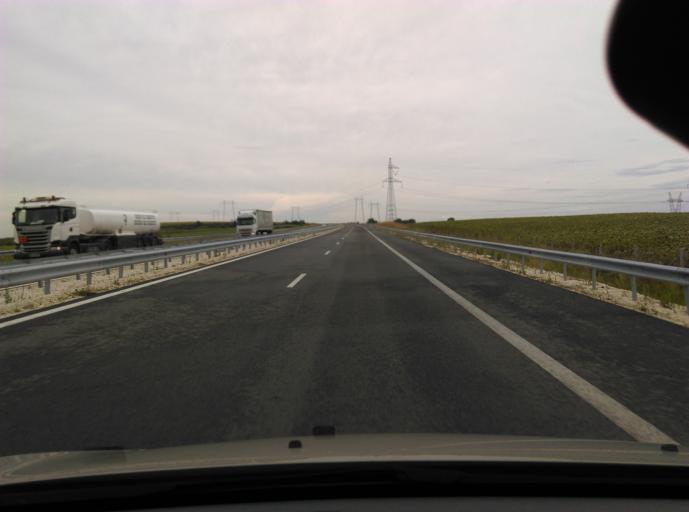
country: BG
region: Stara Zagora
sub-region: Obshtina Chirpan
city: Chirpan
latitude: 42.1260
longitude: 25.3693
